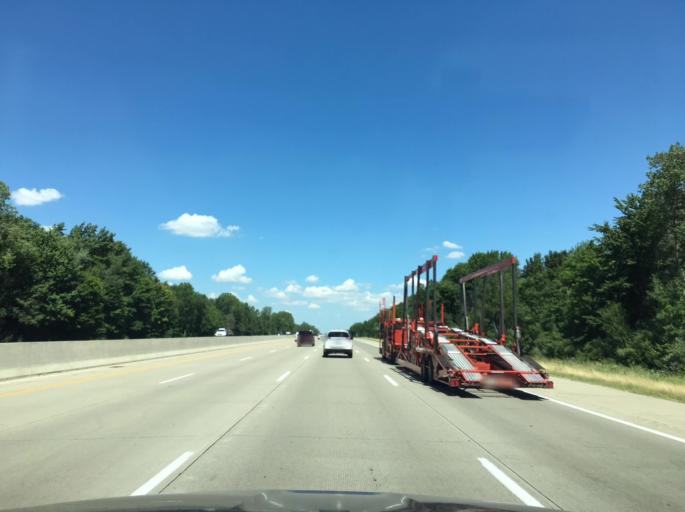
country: US
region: Michigan
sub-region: Saginaw County
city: Bridgeport
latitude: 43.3100
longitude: -83.8382
